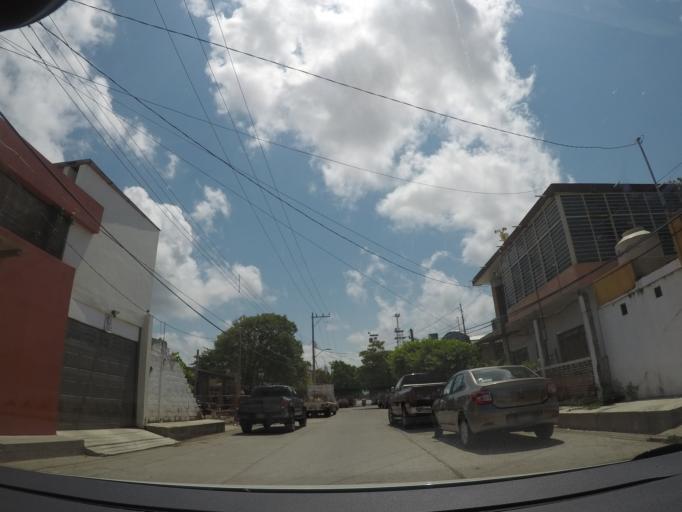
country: MX
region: Oaxaca
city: Juchitan de Zaragoza
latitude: 16.4421
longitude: -95.0184
